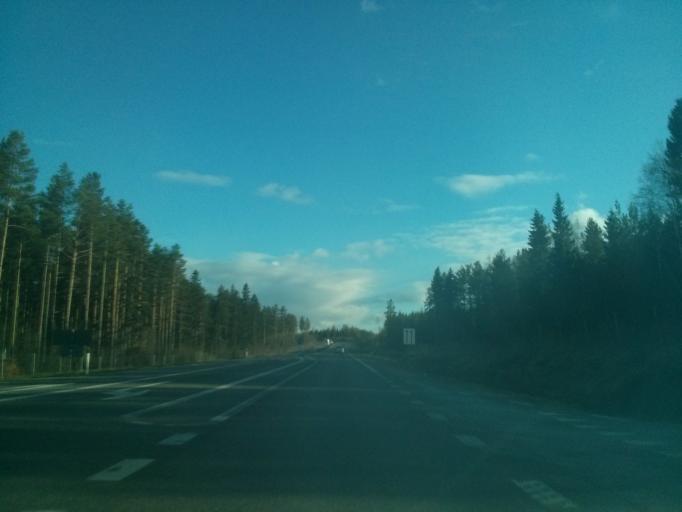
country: SE
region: Vaesternorrland
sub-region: Sundsvalls Kommun
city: Njurundabommen
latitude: 62.1336
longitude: 17.3375
